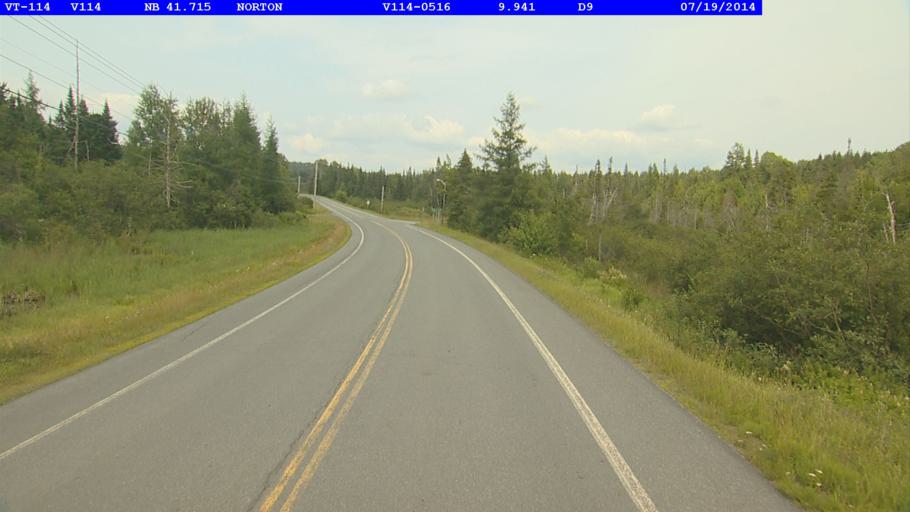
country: CA
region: Quebec
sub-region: Estrie
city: Coaticook
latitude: 44.9990
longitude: -71.7088
